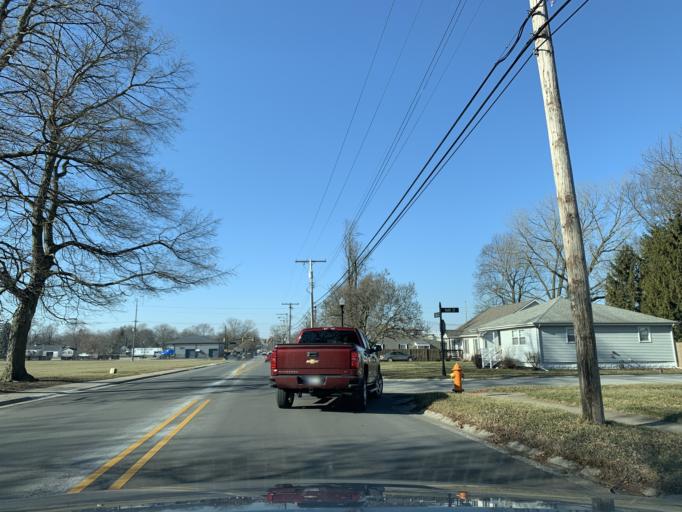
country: US
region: Indiana
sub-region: Lake County
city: Crown Point
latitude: 41.4203
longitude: -87.3526
